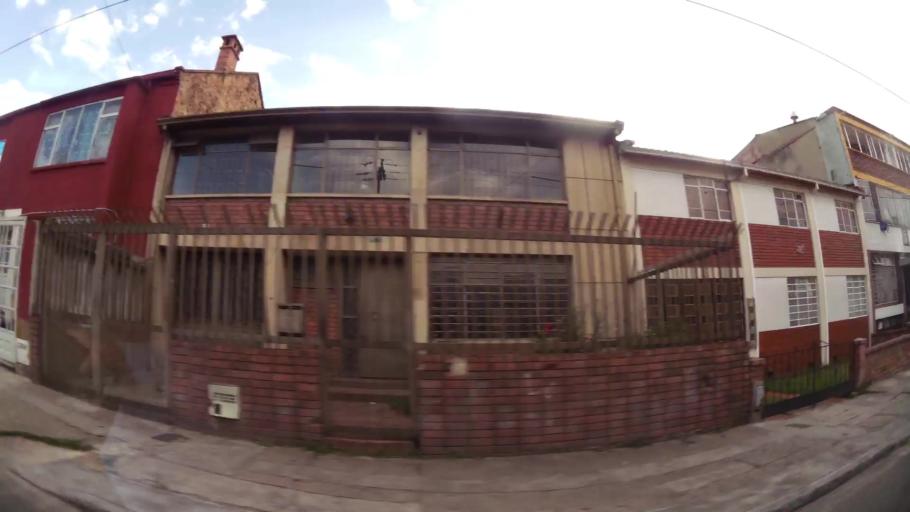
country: CO
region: Bogota D.C.
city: Bogota
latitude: 4.6533
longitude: -74.0666
